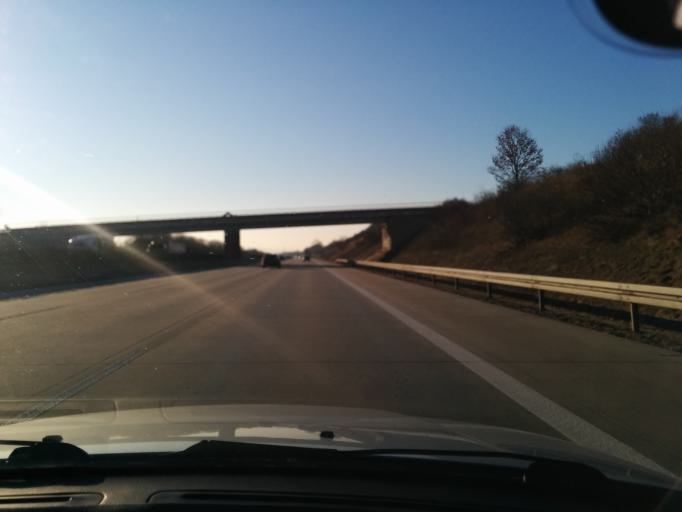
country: DE
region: Thuringia
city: Rockhausen
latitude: 50.9095
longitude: 11.0494
